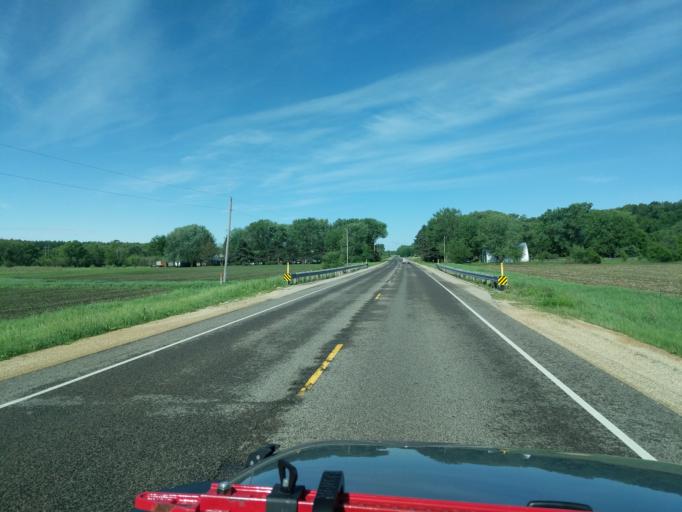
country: US
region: Wisconsin
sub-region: Pierce County
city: River Falls
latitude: 44.8508
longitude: -92.5846
